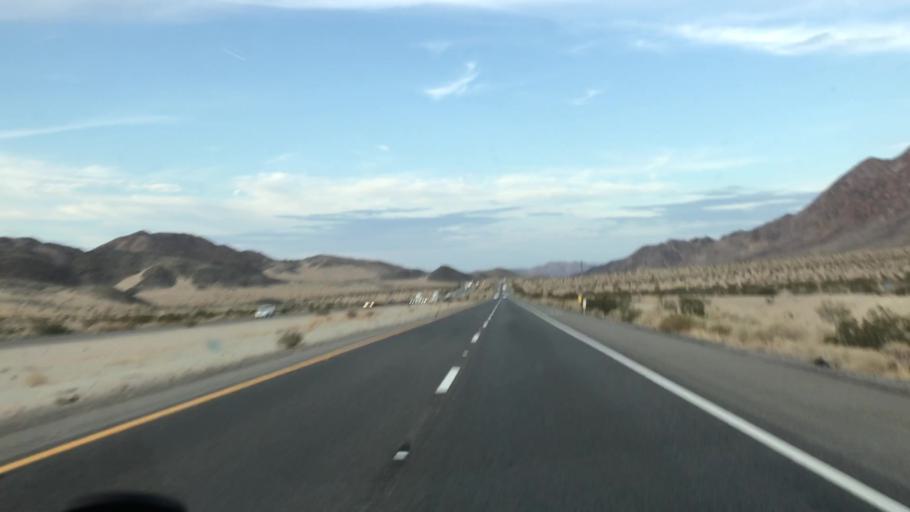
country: US
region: California
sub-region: San Bernardino County
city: Fort Irwin
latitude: 35.0855
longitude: -116.3578
